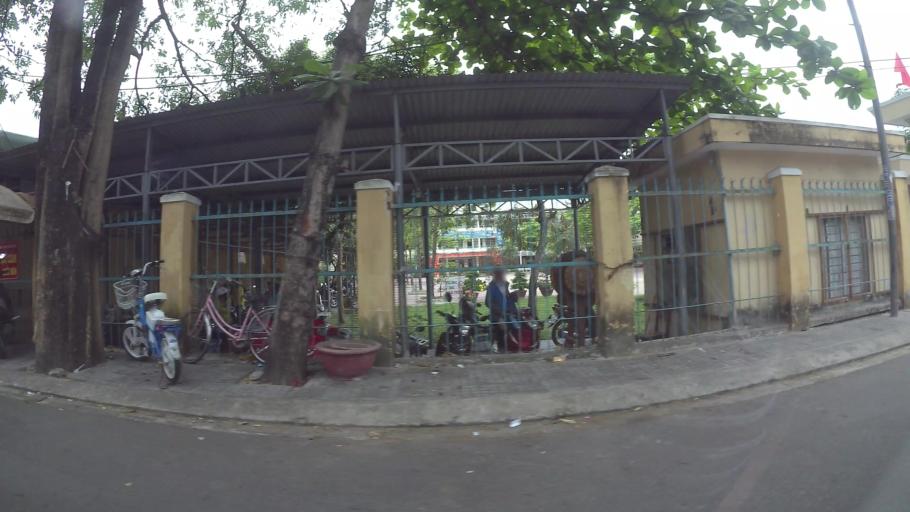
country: VN
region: Da Nang
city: Thanh Khe
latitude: 16.0683
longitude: 108.1847
